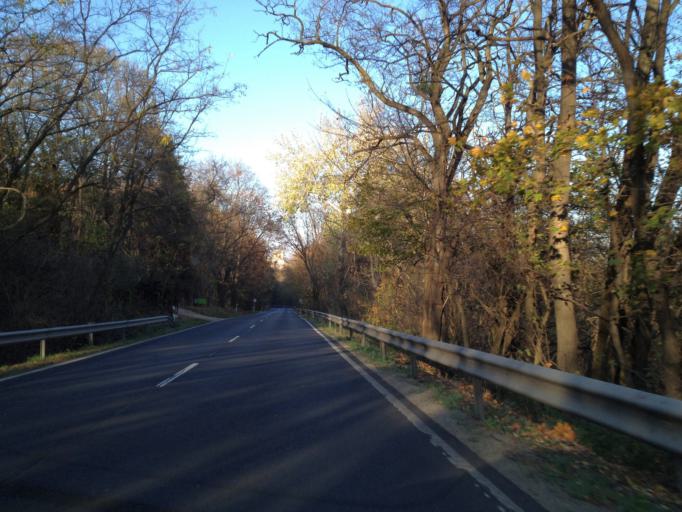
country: HU
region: Veszprem
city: Zirc
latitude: 47.3439
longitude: 17.8793
